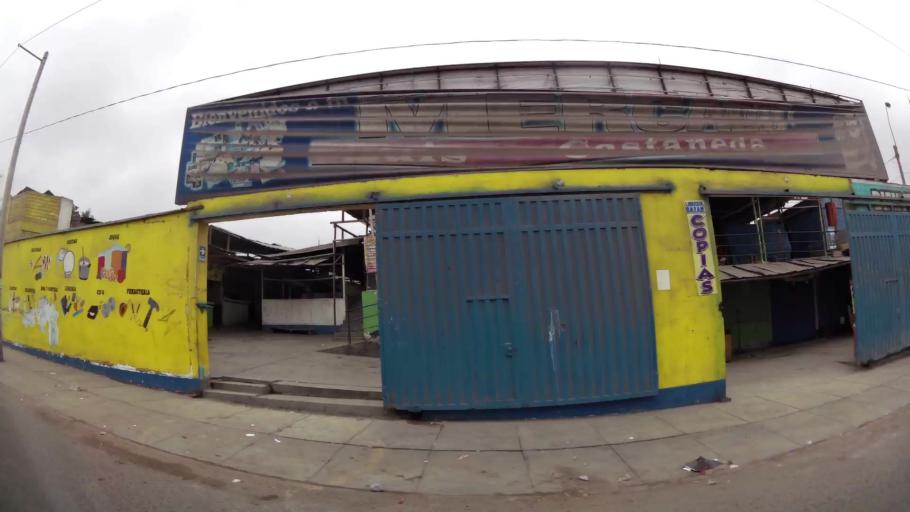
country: PE
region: Lima
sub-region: Lima
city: Surco
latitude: -12.1407
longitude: -76.9658
